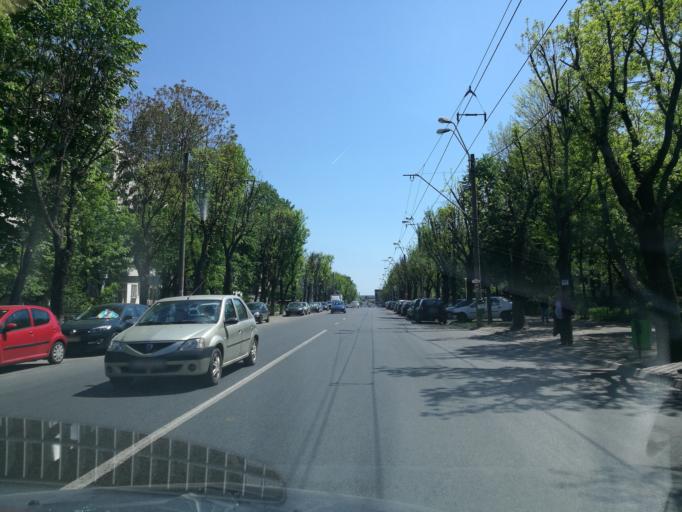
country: RO
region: Ilfov
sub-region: Comuna Popesti-Leordeni
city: Popesti-Leordeni
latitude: 44.3825
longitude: 26.1245
